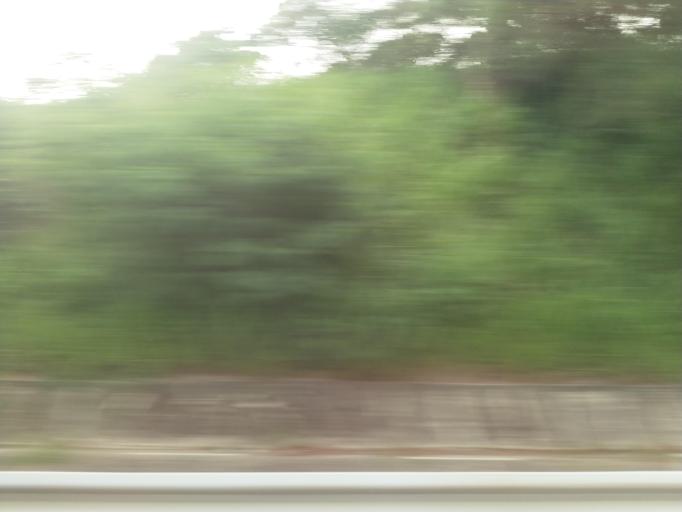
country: TW
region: Taiwan
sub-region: Pingtung
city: Pingtung
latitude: 22.7788
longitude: 120.4220
